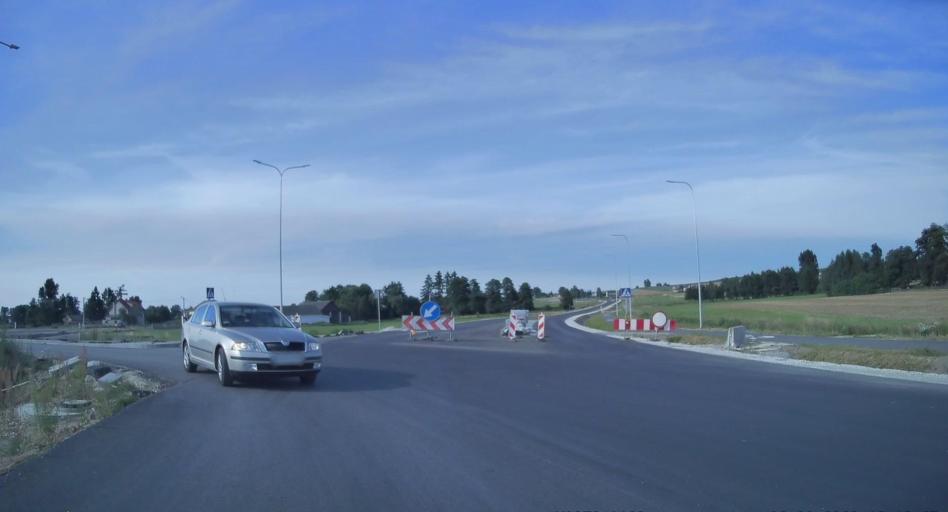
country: PL
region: Swietokrzyskie
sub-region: Powiat kielecki
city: Lopuszno
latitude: 50.9662
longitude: 20.2459
